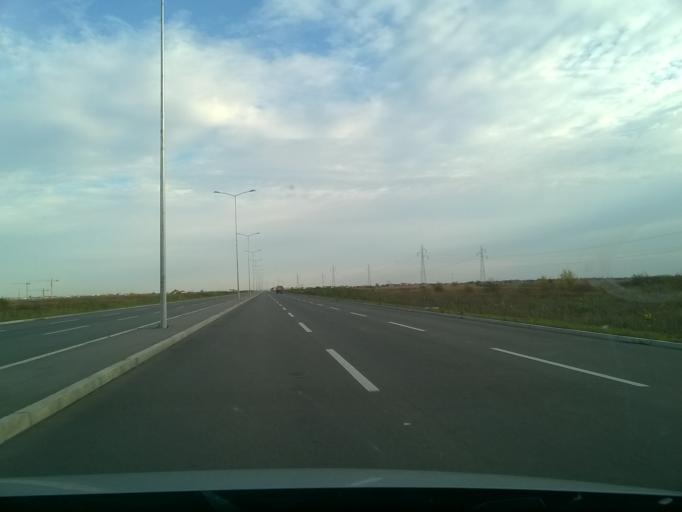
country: RS
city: Ovca
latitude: 44.8721
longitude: 20.5166
